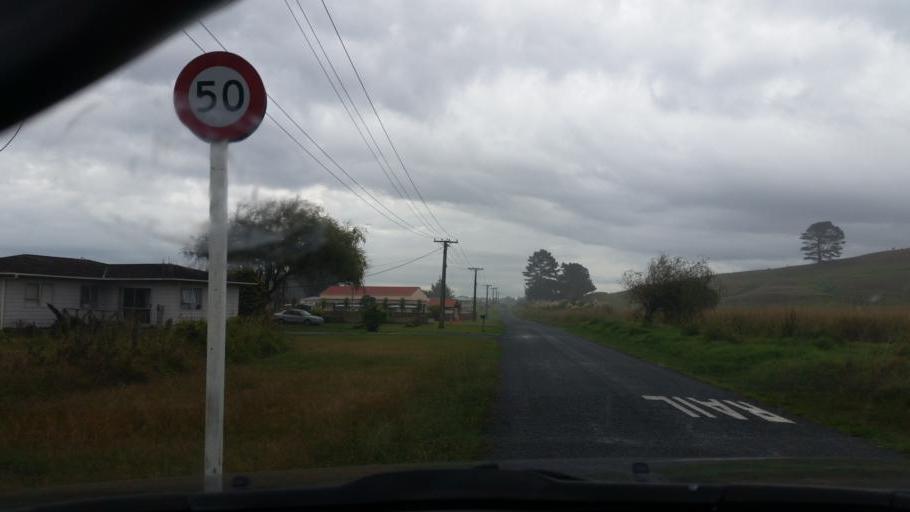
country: NZ
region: Northland
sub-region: Kaipara District
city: Dargaville
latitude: -35.9363
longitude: 173.8520
